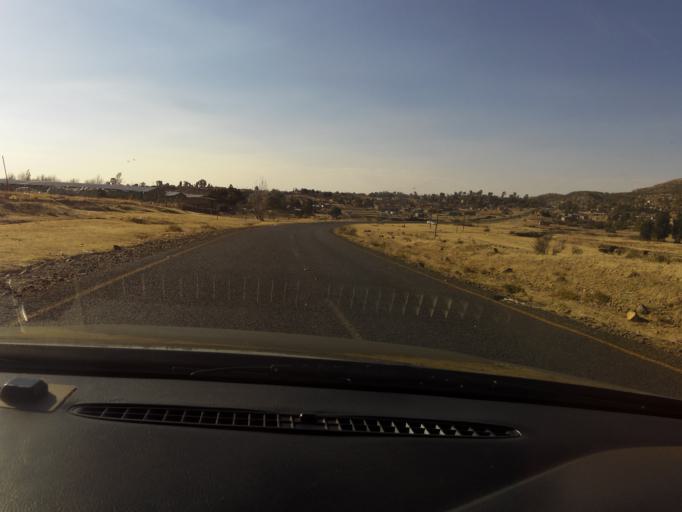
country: LS
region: Mafeteng
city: Mafeteng
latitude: -29.8478
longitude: 27.2293
